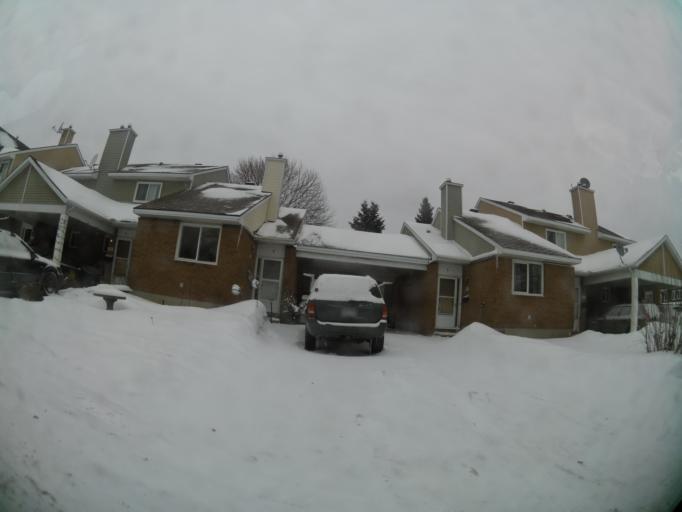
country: CA
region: Ontario
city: Ottawa
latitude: 45.3710
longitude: -75.6210
